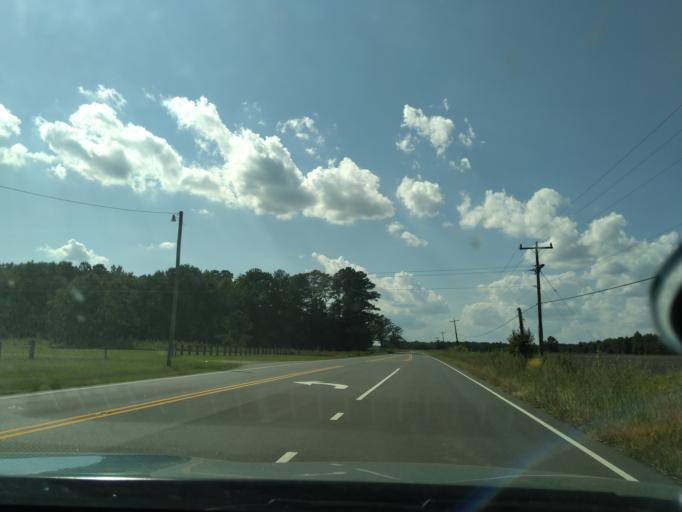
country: US
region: North Carolina
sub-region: Martin County
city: Robersonville
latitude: 35.8253
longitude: -77.2777
